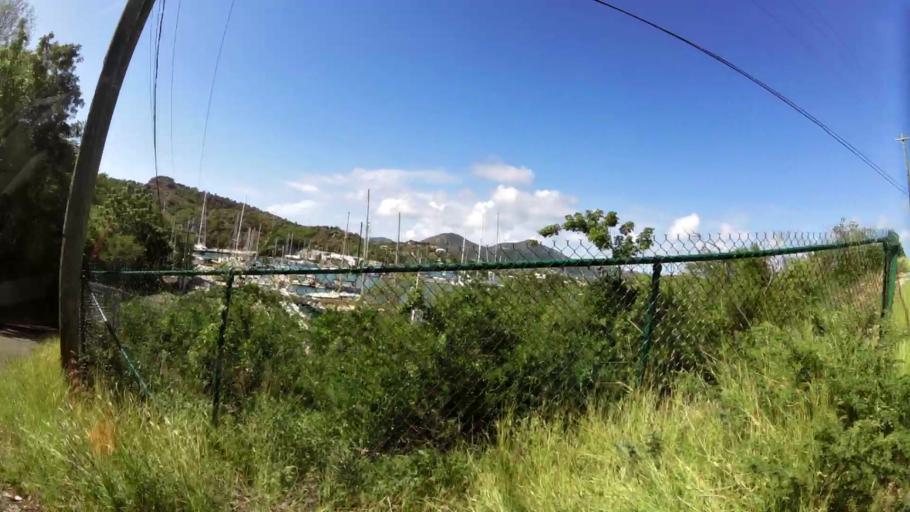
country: AG
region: Saint Paul
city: Falmouth
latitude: 17.0079
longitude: -61.7612
